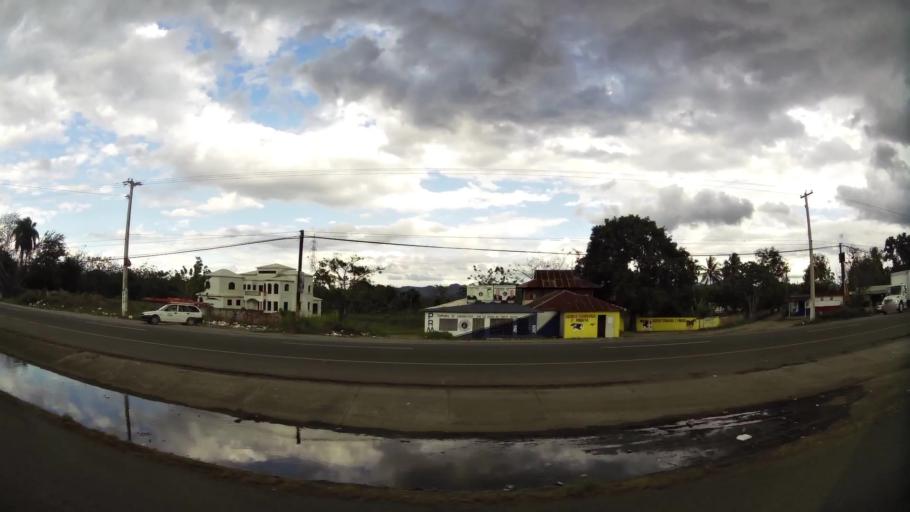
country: DO
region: Monsenor Nouel
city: Sabana del Puerto
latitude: 19.0492
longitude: -70.4461
